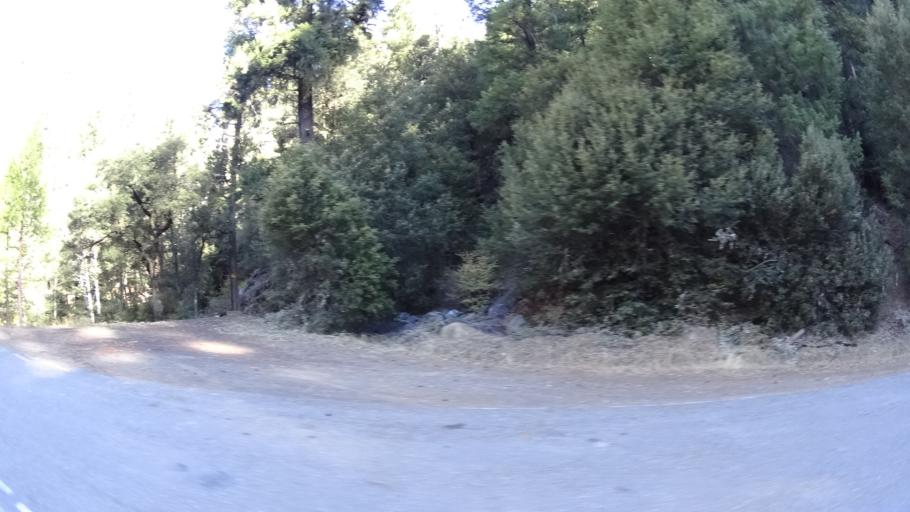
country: US
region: California
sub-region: Trinity County
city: Weaverville
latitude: 41.2275
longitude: -123.0160
